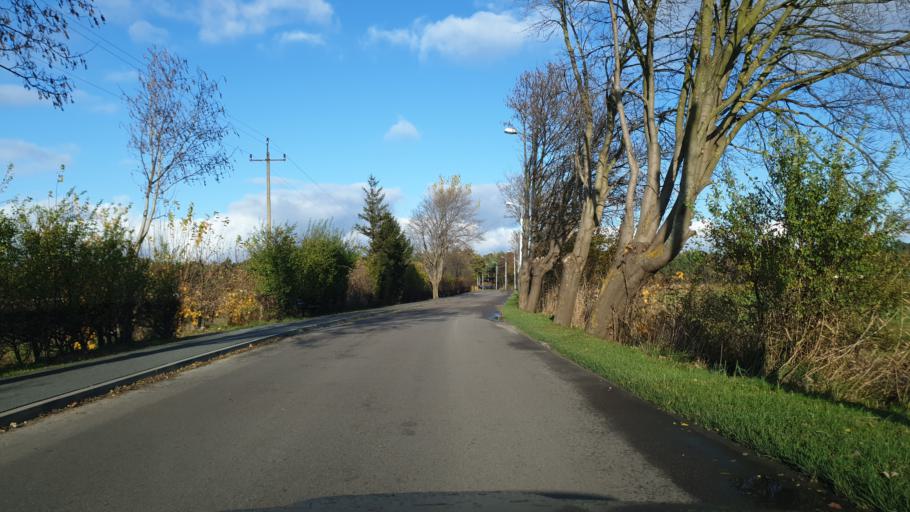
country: PL
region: Pomeranian Voivodeship
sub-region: Powiat pucki
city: Jastrzebia Gora
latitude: 54.8273
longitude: 18.2440
